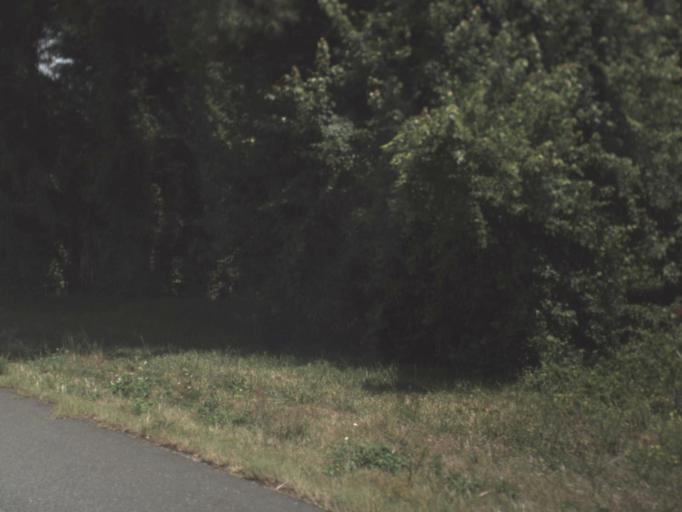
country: US
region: Florida
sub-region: Saint Johns County
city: Palm Valley
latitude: 30.1718
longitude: -81.3733
